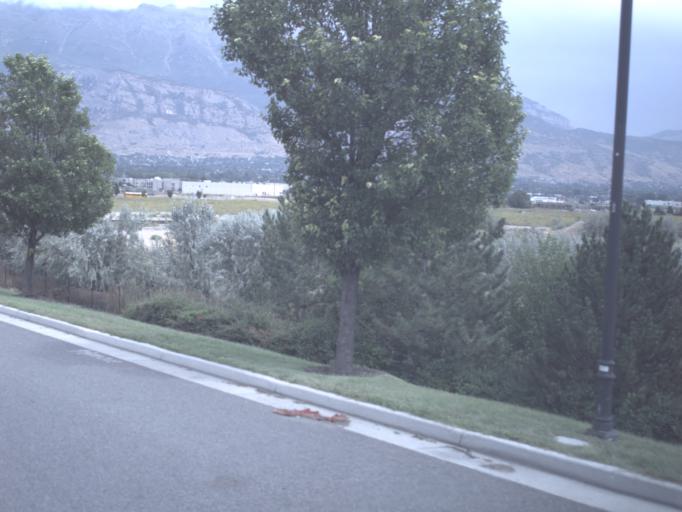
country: US
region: Utah
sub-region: Utah County
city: Pleasant Grove
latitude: 40.3512
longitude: -111.7670
